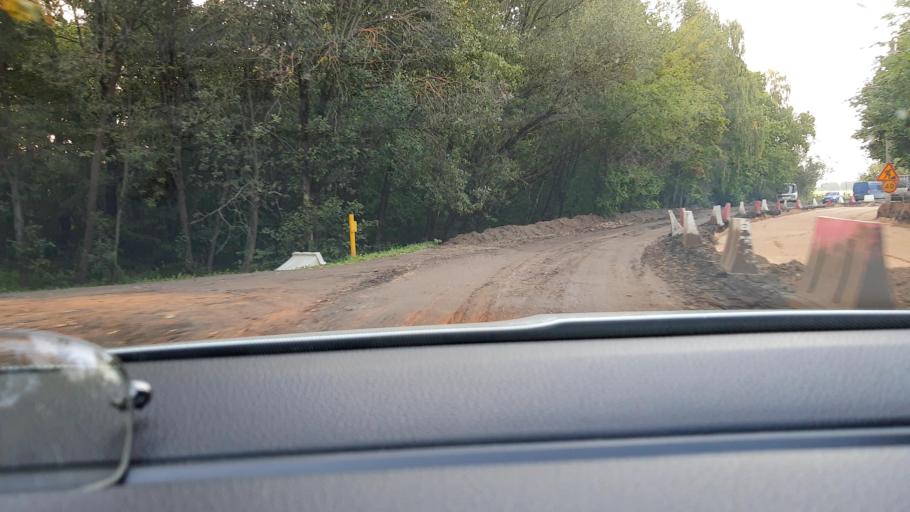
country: RU
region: Moskovskaya
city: Troitsk
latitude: 55.3142
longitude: 37.1746
